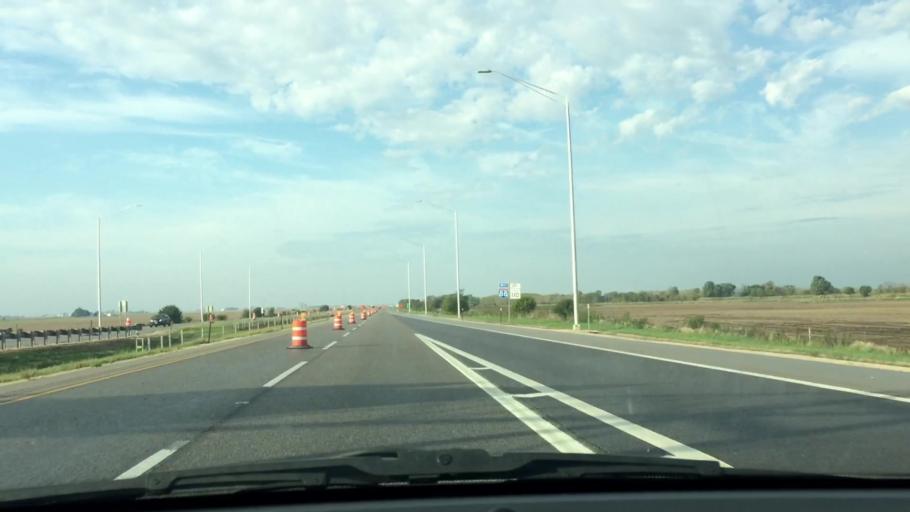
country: US
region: Illinois
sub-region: Ogle County
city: Rochelle
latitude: 41.8984
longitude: -89.0771
